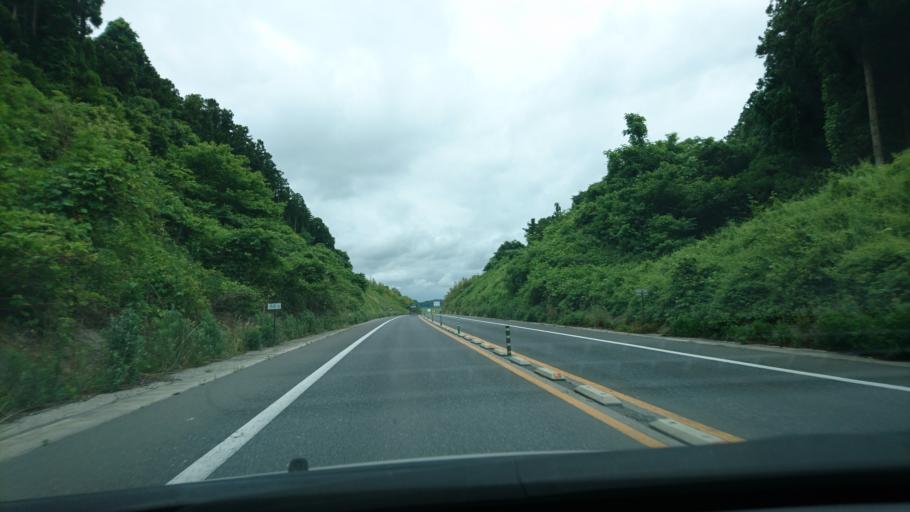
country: JP
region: Miyagi
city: Wakuya
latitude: 38.5921
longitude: 141.2801
